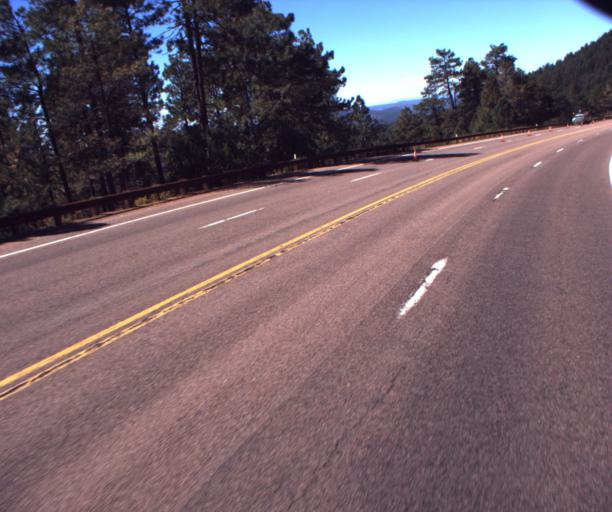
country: US
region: Arizona
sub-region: Gila County
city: Star Valley
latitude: 34.3049
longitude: -110.9251
